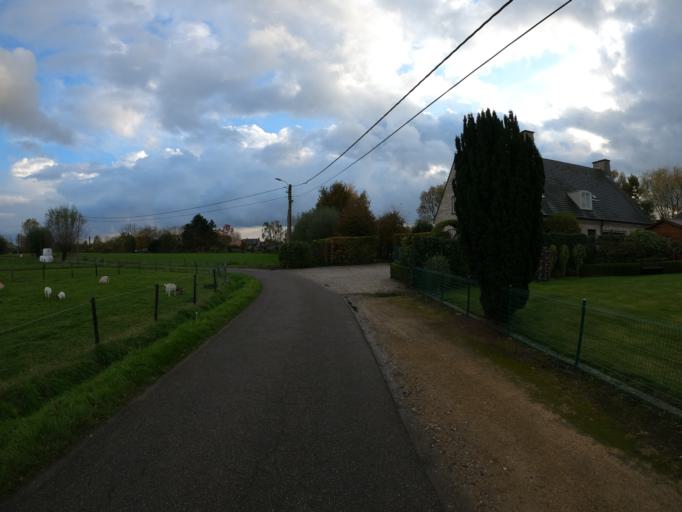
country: BE
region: Flanders
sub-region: Provincie Oost-Vlaanderen
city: Hamme
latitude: 51.1201
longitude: 4.1558
